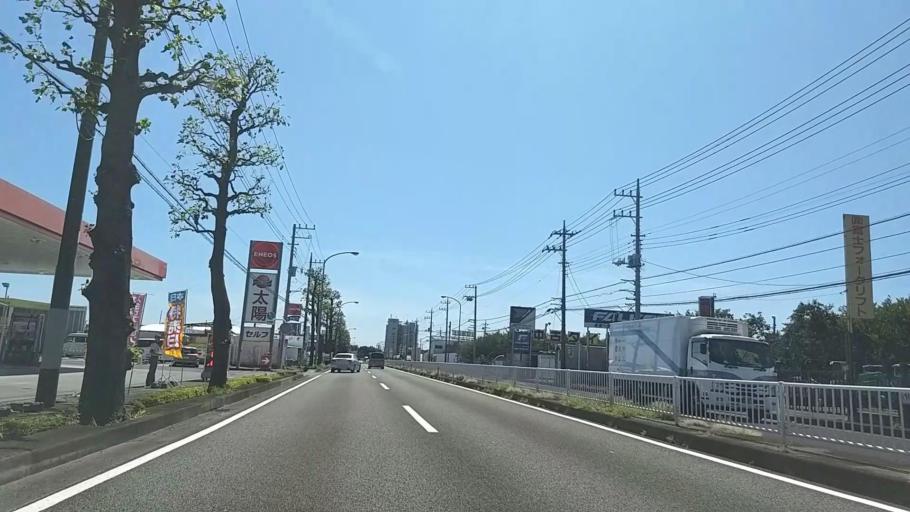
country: JP
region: Kanagawa
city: Zama
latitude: 35.5463
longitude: 139.3576
